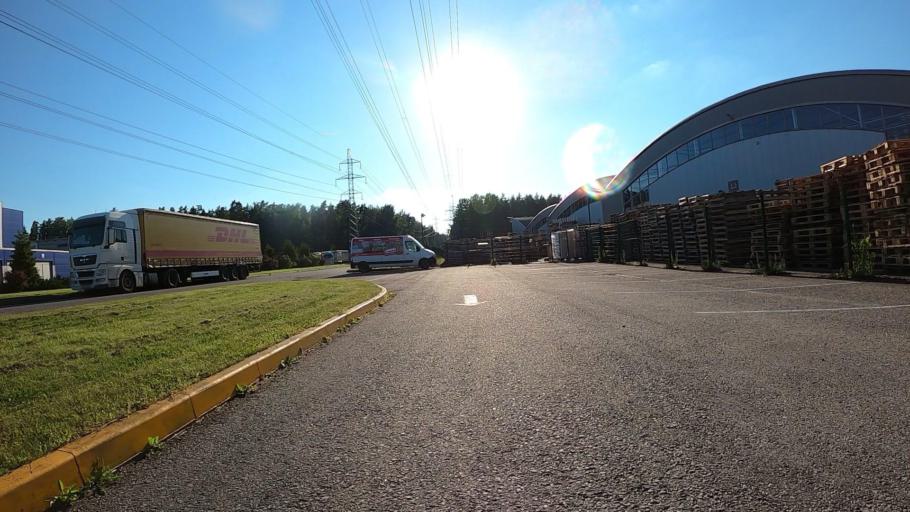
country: LV
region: Stopini
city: Ulbroka
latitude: 56.9294
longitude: 24.2393
